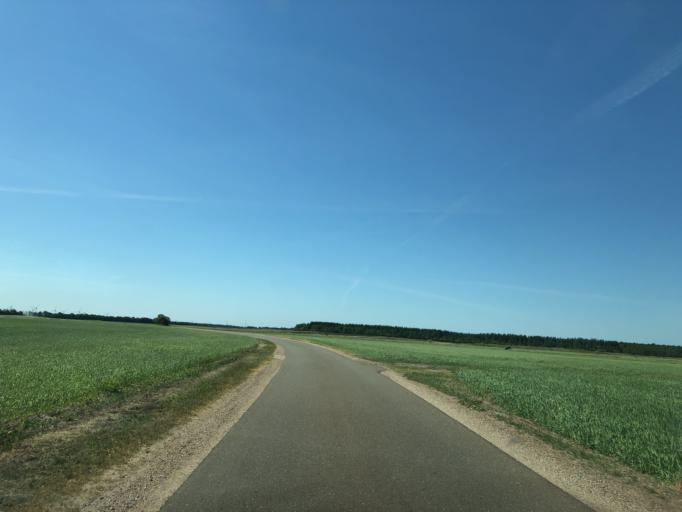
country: DK
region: Central Jutland
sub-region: Struer Kommune
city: Struer
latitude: 56.4185
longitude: 8.4297
